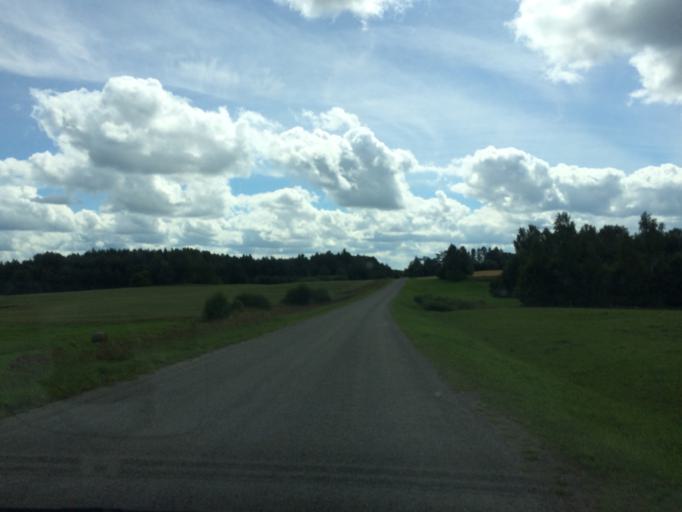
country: LV
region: Karsava
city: Karsava
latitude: 56.6442
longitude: 27.5120
